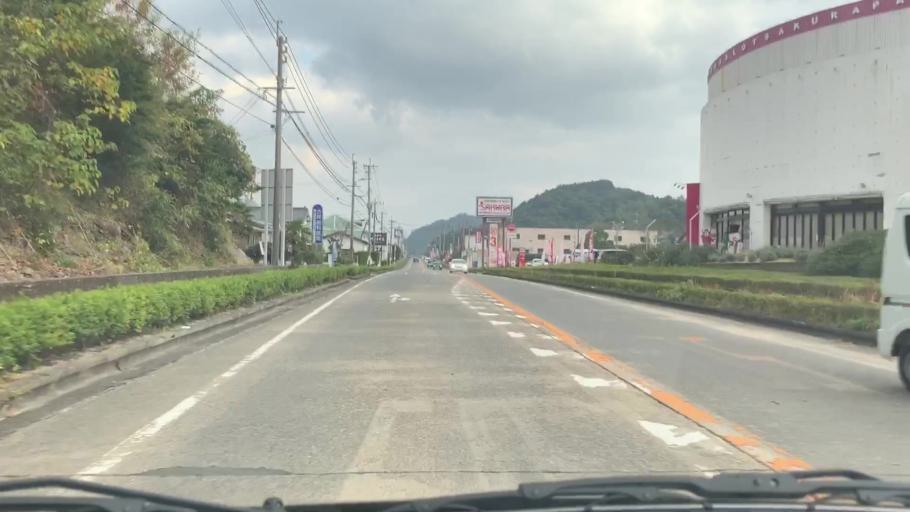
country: JP
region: Saga Prefecture
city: Imaricho-ko
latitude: 33.1857
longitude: 129.8690
